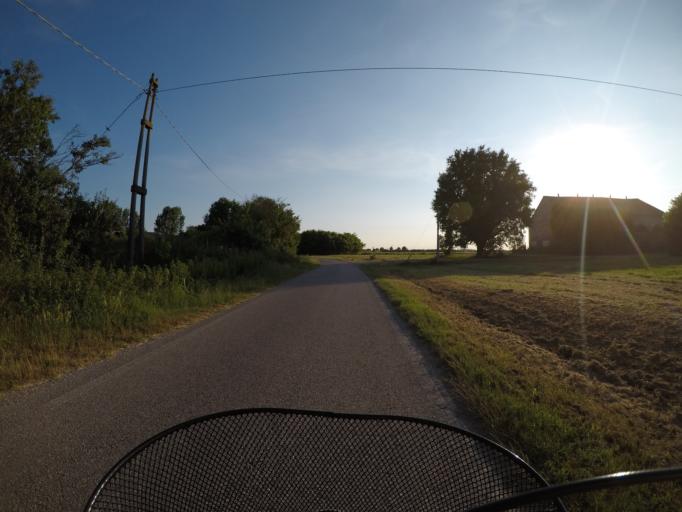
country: IT
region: Veneto
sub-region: Provincia di Rovigo
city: Pincara
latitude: 45.0204
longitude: 11.6155
